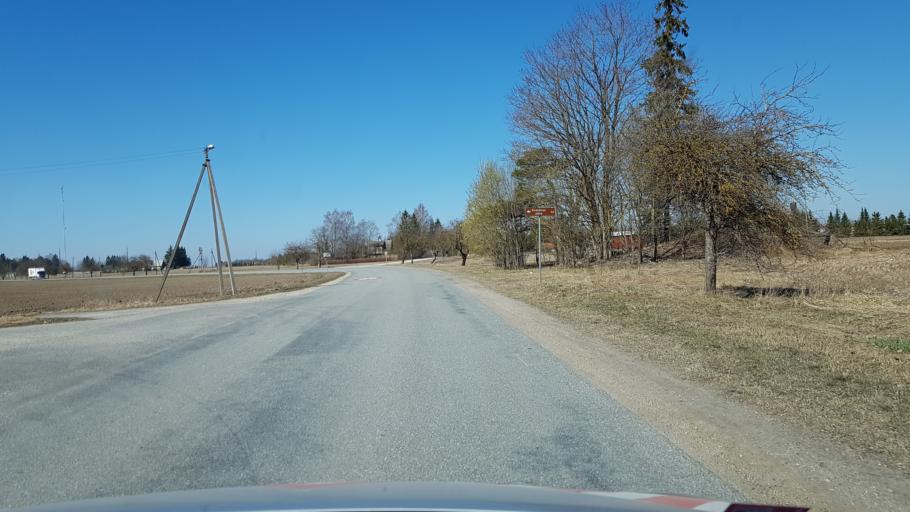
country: EE
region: Laeaene-Virumaa
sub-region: Rakke vald
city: Rakke
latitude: 59.0481
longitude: 26.3934
